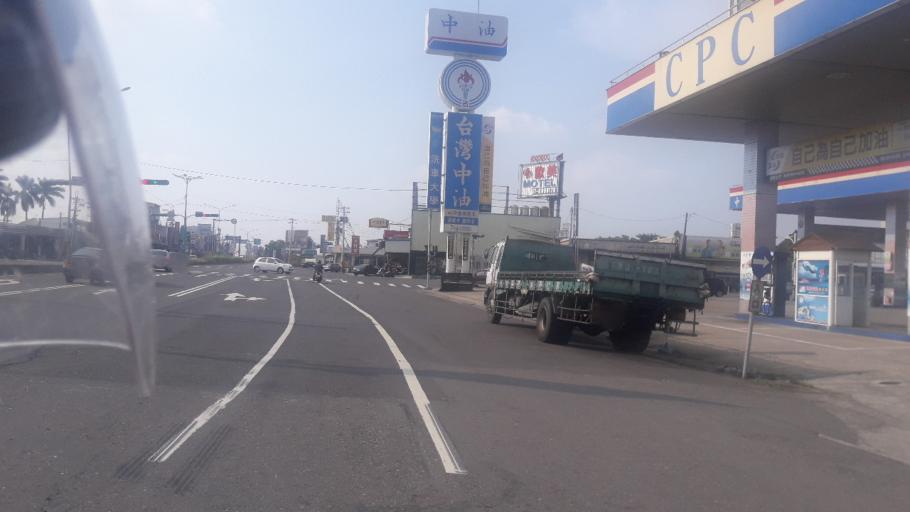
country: TW
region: Taiwan
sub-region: Tainan
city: Tainan
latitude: 22.8801
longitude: 120.2506
